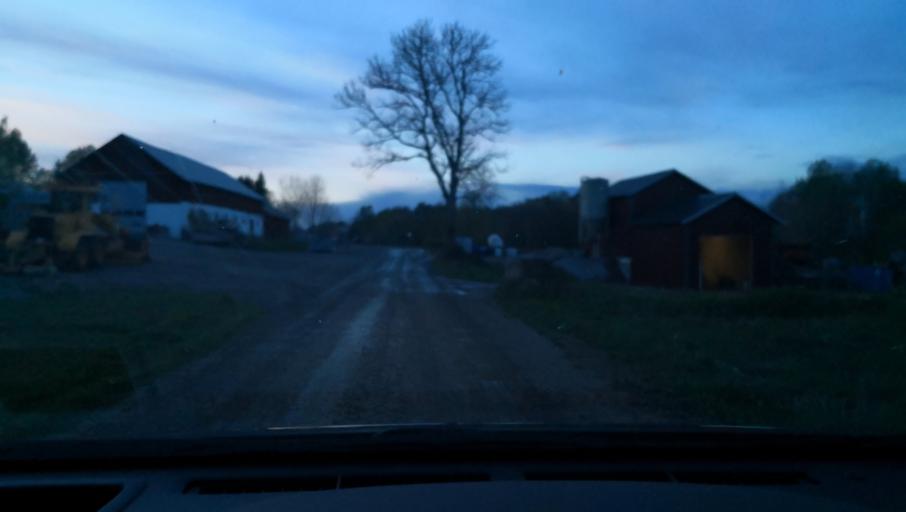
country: SE
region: OErebro
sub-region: Askersunds Kommun
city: Askersund
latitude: 58.9947
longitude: 14.9029
